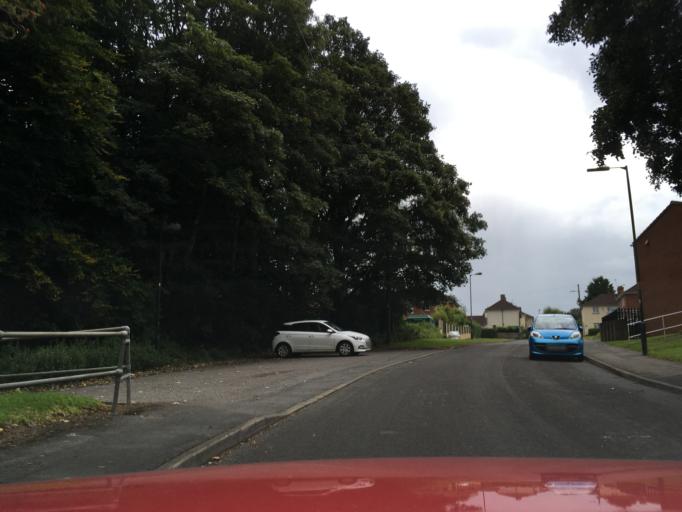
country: GB
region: England
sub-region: South Gloucestershire
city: Kingswood
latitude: 51.4504
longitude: -2.5384
